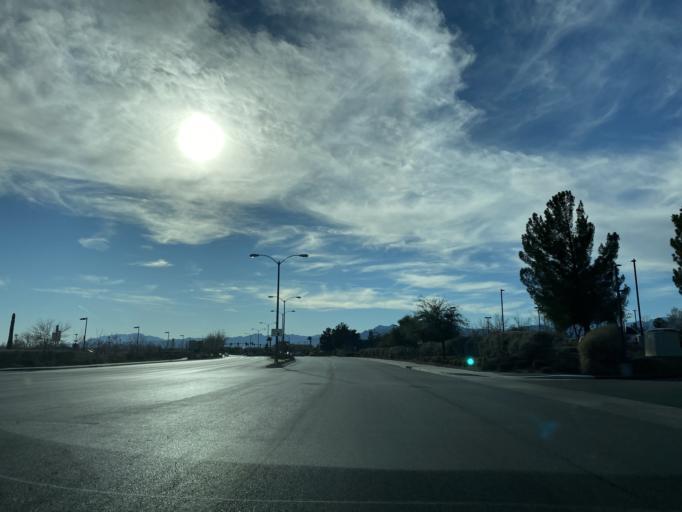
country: US
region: Nevada
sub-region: Clark County
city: North Las Vegas
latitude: 36.2943
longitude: -115.1814
